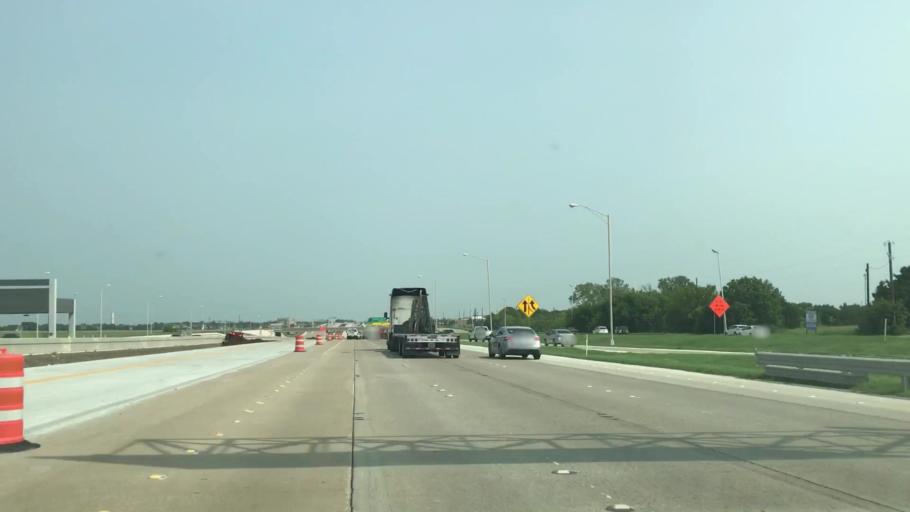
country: US
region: Texas
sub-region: Collin County
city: Murphy
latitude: 32.9731
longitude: -96.6538
